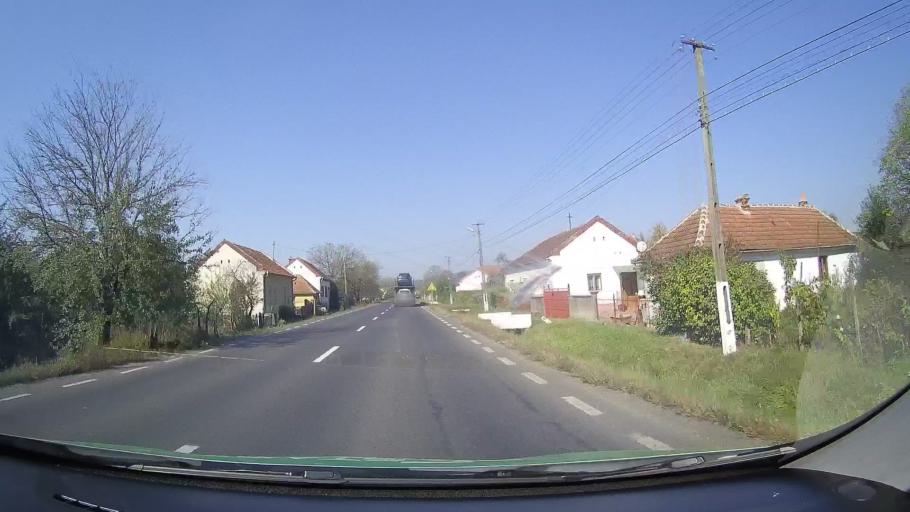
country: RO
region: Arad
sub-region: Comuna Varadia de Mures
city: Varadia de Mures
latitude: 46.0071
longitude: 22.1528
